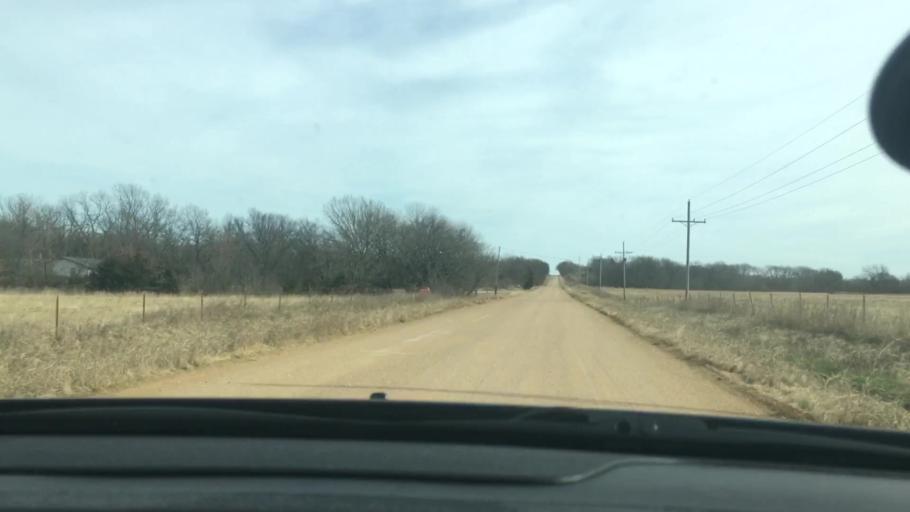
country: US
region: Oklahoma
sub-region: Murray County
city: Sulphur
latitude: 34.4049
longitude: -96.9091
